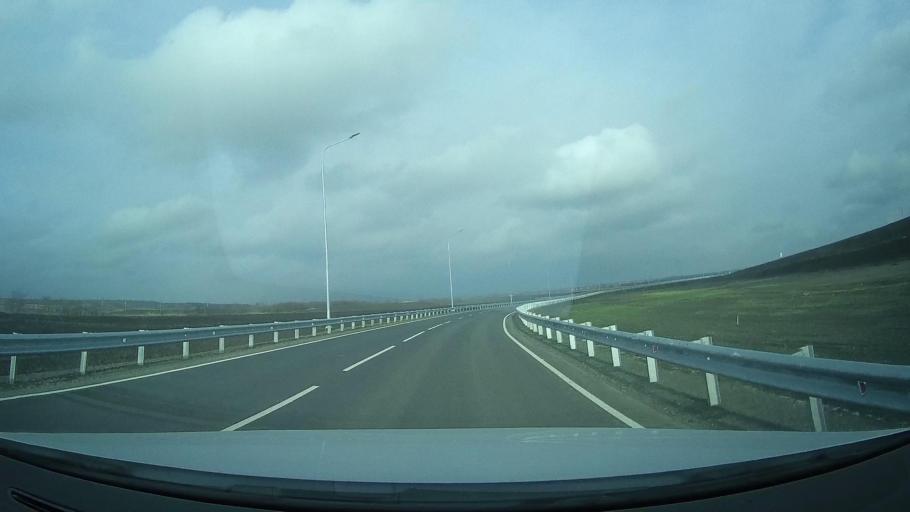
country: RU
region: Rostov
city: Grushevskaya
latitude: 47.4546
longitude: 39.8828
